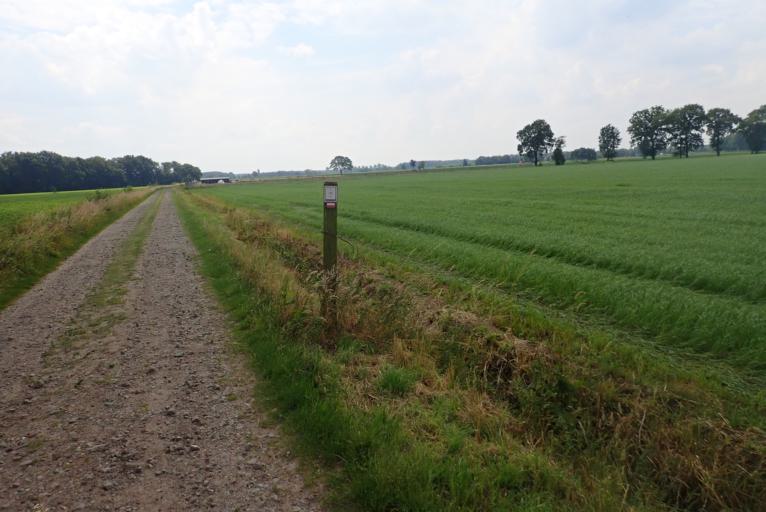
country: BE
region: Flanders
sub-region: Provincie Antwerpen
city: Brecht
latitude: 51.3185
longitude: 4.6426
